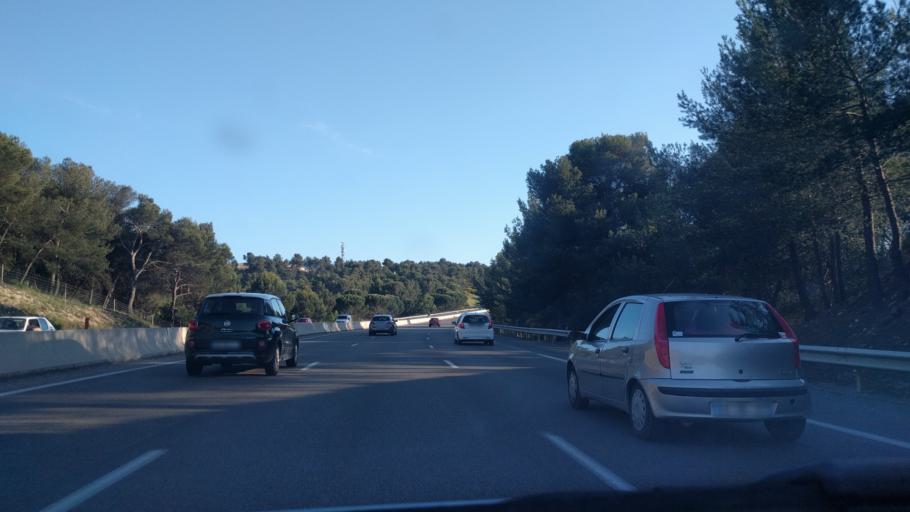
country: FR
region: Provence-Alpes-Cote d'Azur
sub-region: Departement des Bouches-du-Rhone
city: Venelles
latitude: 43.6030
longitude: 5.4965
